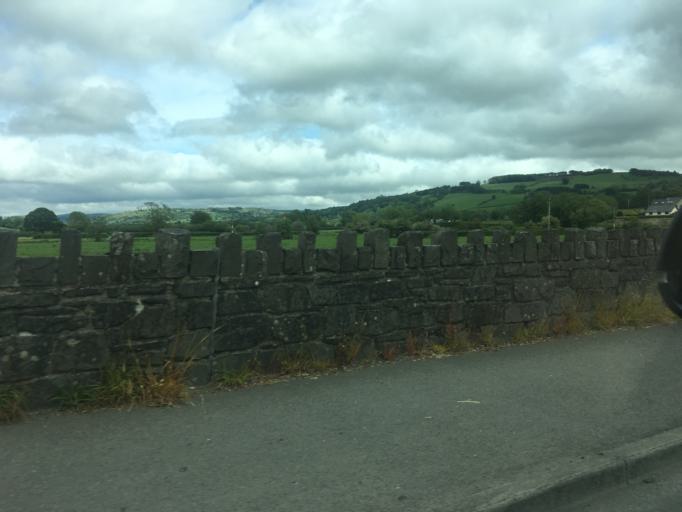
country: GB
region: Wales
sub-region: County of Ceredigion
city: Lampeter
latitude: 52.1077
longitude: -4.0720
